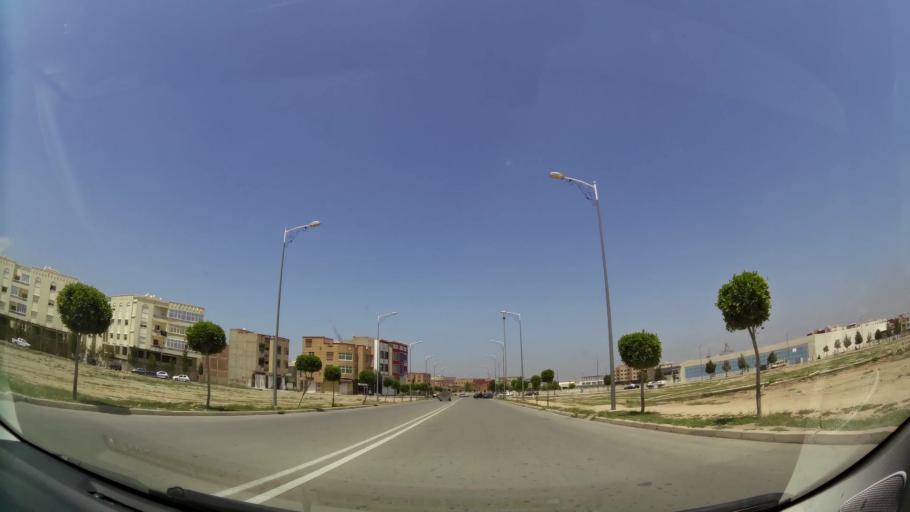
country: MA
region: Oriental
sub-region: Oujda-Angad
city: Oujda
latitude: 34.6963
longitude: -1.8927
